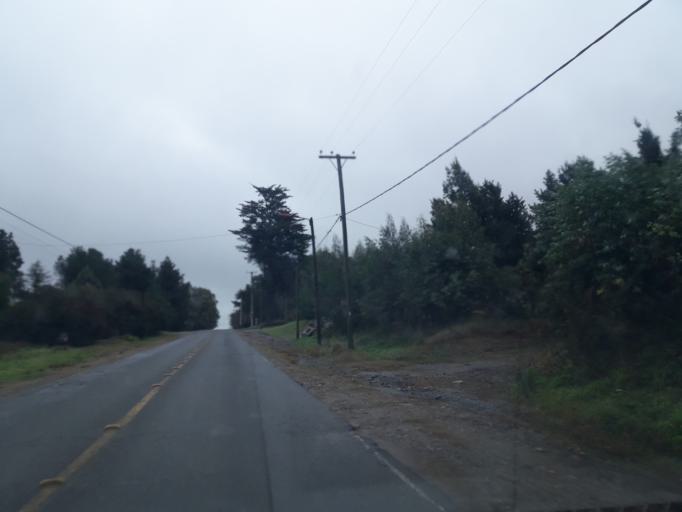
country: AR
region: Buenos Aires
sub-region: Partido de Tandil
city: Tandil
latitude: -37.3290
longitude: -59.1762
